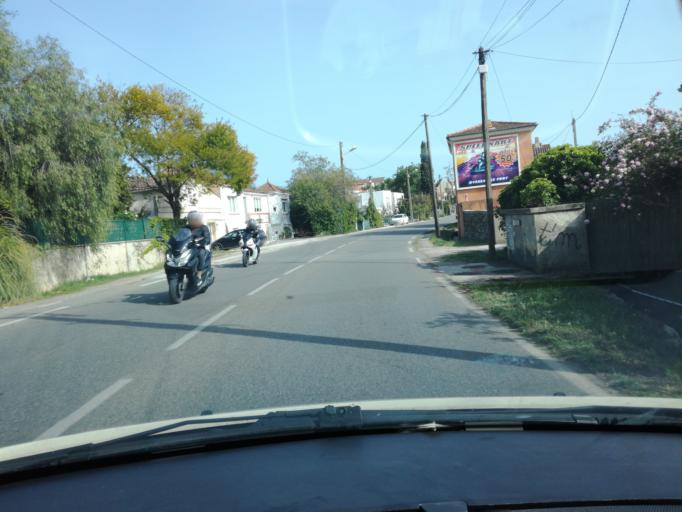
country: FR
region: Provence-Alpes-Cote d'Azur
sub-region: Departement du Var
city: Hyeres
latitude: 43.1253
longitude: 6.1134
